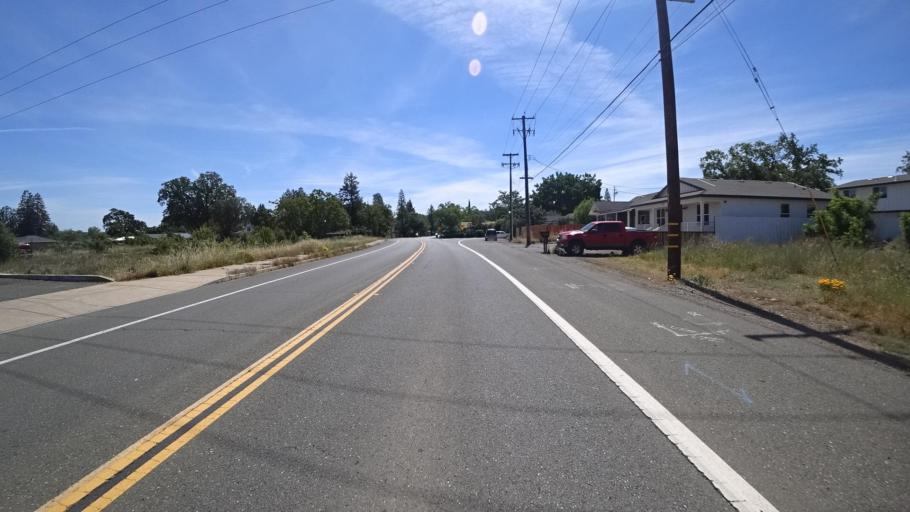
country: US
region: California
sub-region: Lake County
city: Middletown
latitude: 38.7531
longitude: -122.6187
